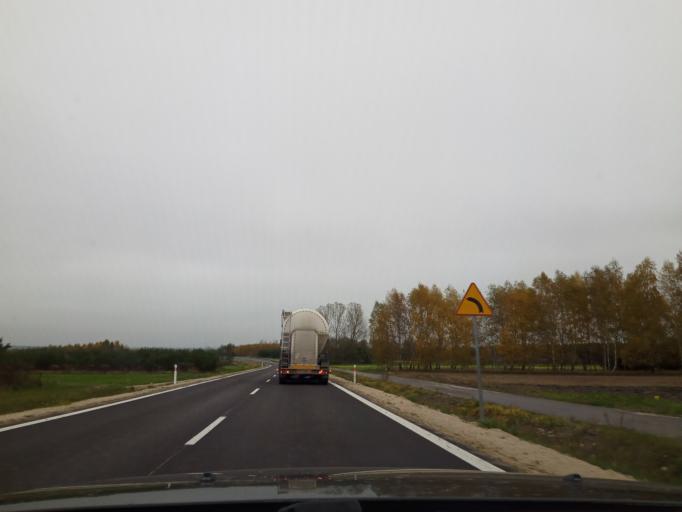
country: PL
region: Swietokrzyskie
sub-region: Powiat jedrzejowski
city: Jedrzejow
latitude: 50.6229
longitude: 20.3202
